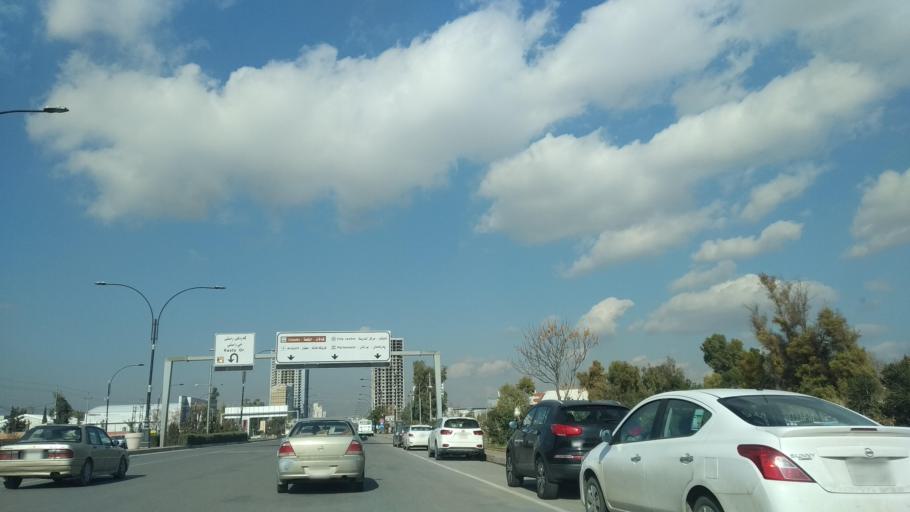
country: IQ
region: Arbil
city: Erbil
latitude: 36.1406
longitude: 44.0208
